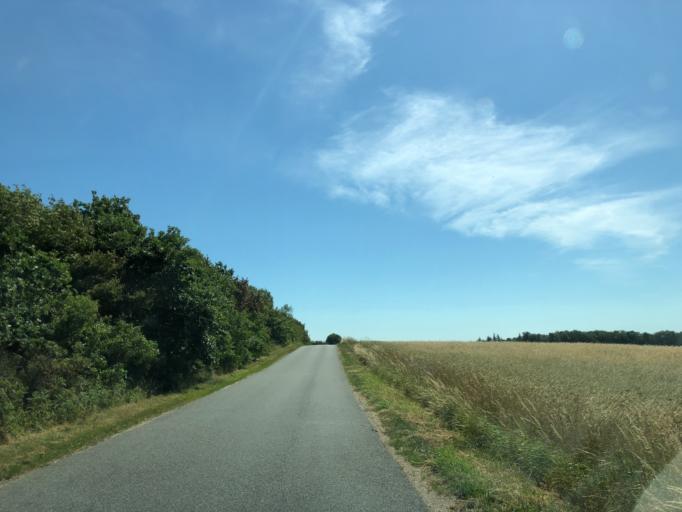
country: DK
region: Central Jutland
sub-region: Skive Kommune
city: Skive
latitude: 56.4832
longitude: 8.9981
